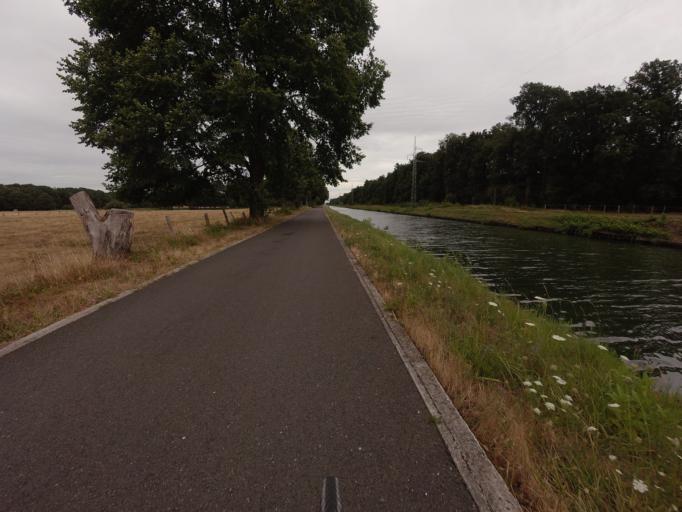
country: BE
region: Flanders
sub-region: Provincie Antwerpen
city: Brecht
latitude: 51.3207
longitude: 4.6150
